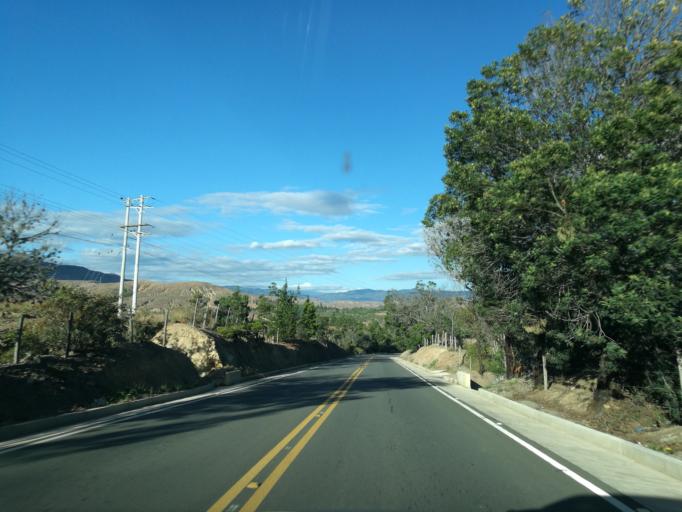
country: CO
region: Boyaca
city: Villa de Leiva
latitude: 5.6240
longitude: -73.5739
